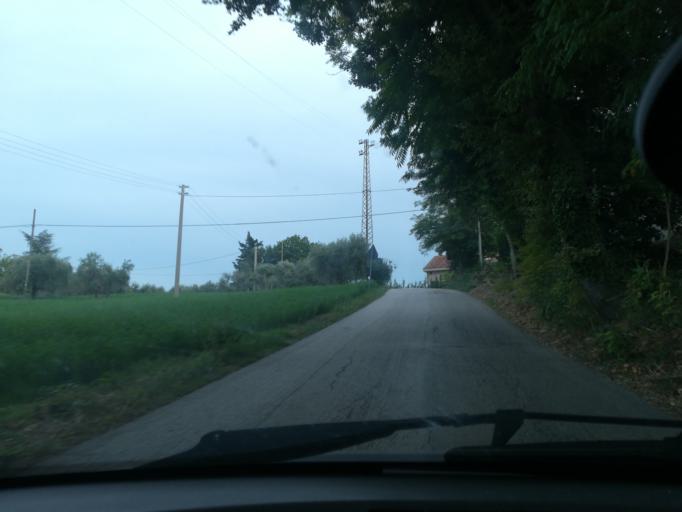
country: IT
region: The Marches
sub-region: Provincia di Macerata
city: Piediripa
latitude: 43.2969
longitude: 13.4825
